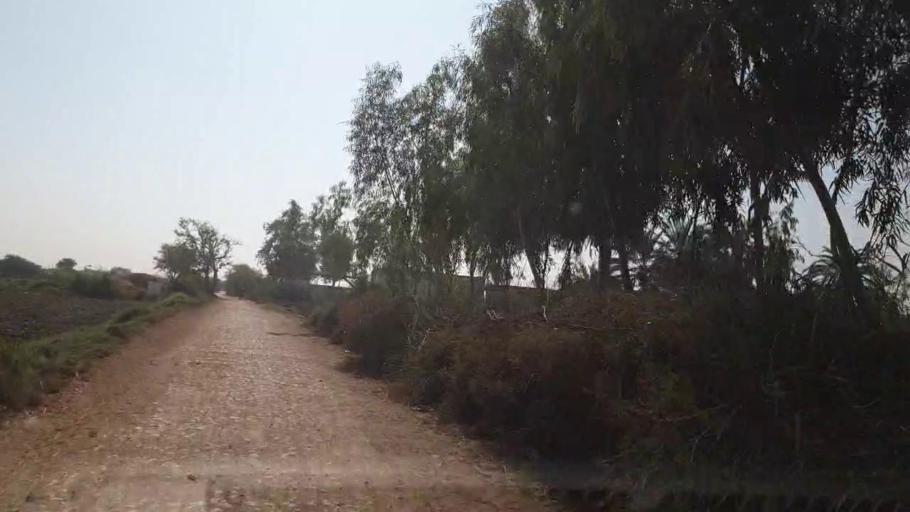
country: PK
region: Sindh
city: Gharo
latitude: 24.6792
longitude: 67.7500
